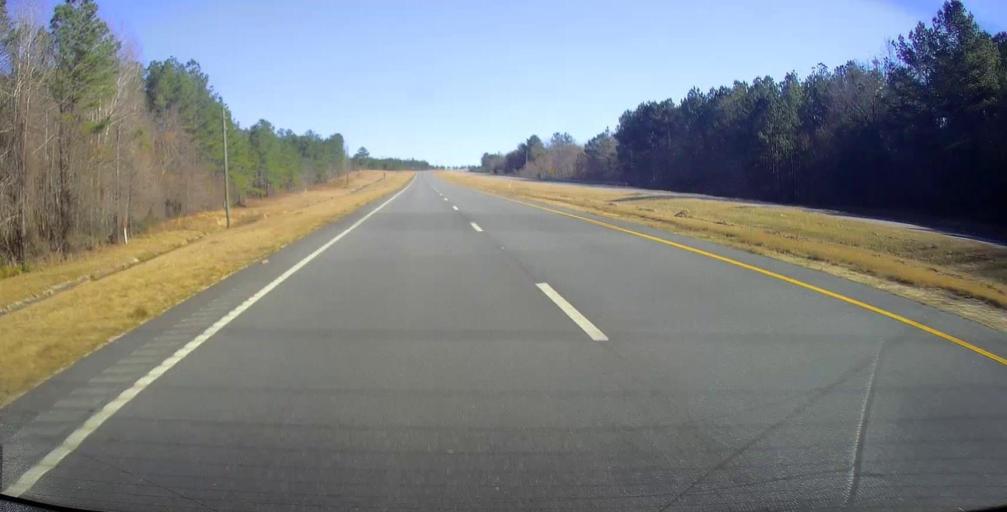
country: US
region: Georgia
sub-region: Taylor County
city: Butler
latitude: 32.6152
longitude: -84.2423
